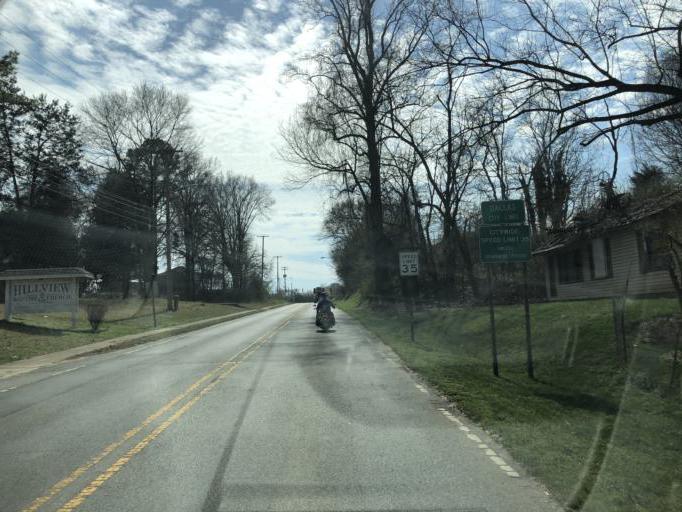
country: US
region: North Carolina
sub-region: Gaston County
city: Dallas
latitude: 35.3182
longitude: -81.1669
